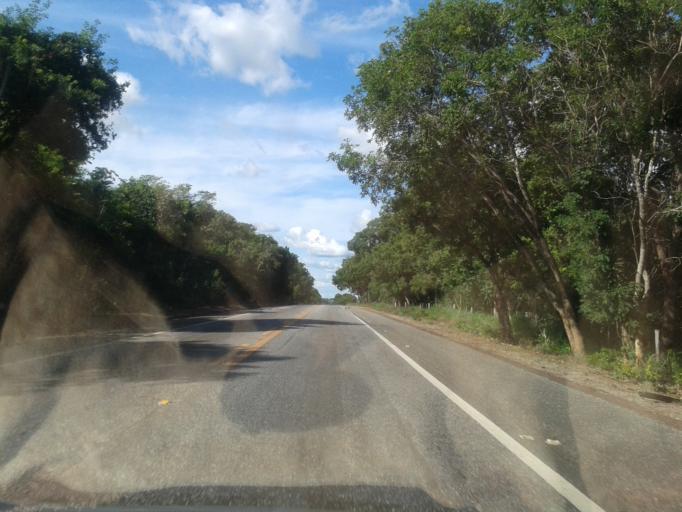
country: BR
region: Goias
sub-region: Mozarlandia
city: Mozarlandia
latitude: -14.8571
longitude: -50.5459
